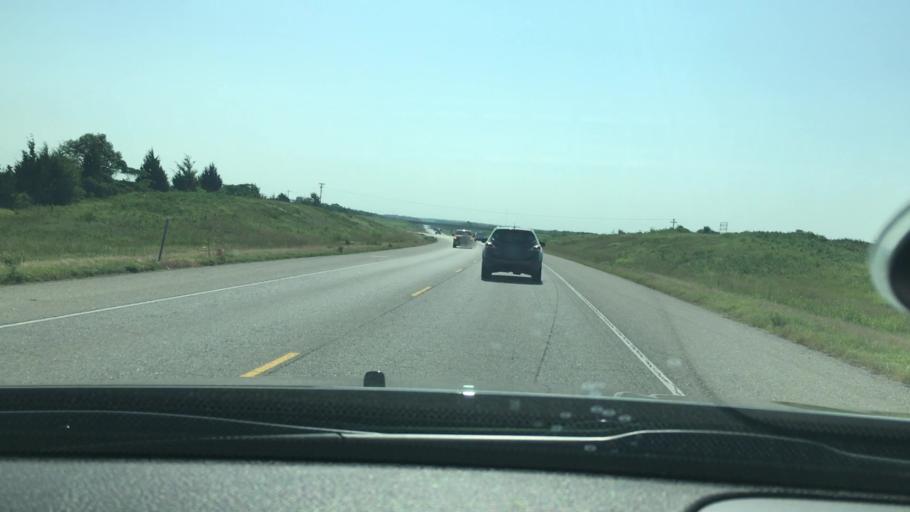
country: US
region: Oklahoma
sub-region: Pontotoc County
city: Ada
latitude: 34.6424
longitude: -96.5392
